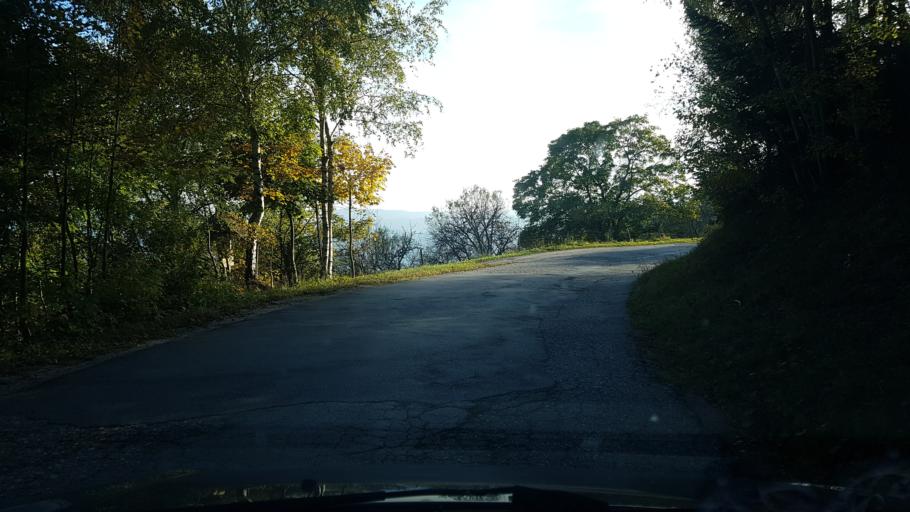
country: SI
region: Slovenj Gradec
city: Legen
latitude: 46.4874
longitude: 15.1781
